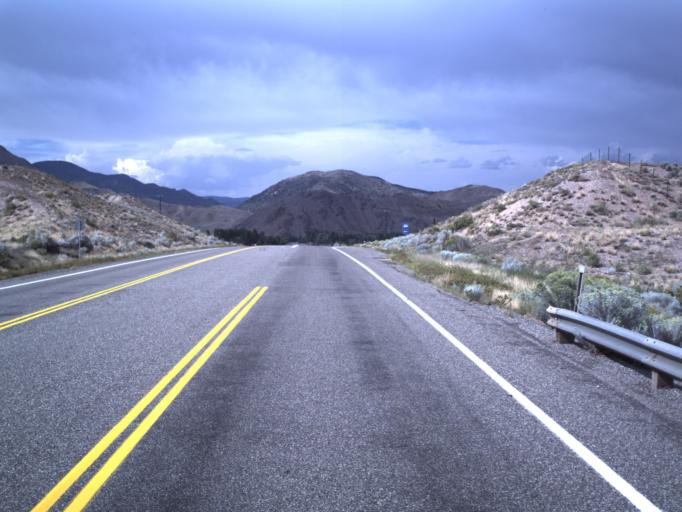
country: US
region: Utah
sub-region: Sevier County
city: Monroe
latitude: 38.4588
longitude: -112.2315
